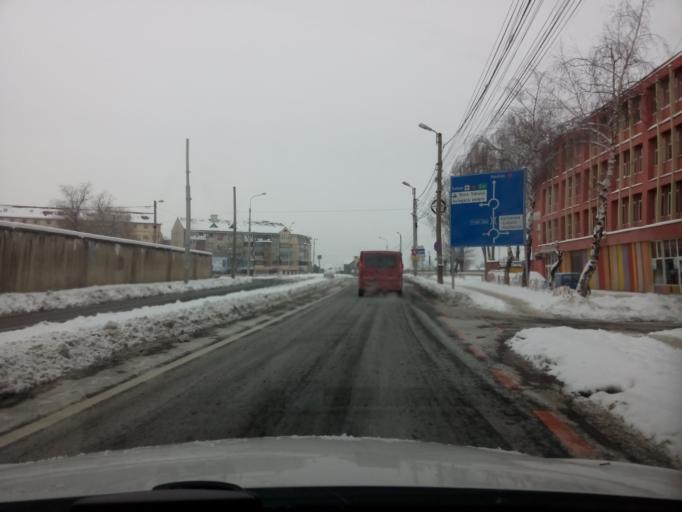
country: RO
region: Sibiu
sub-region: Municipiul Sibiu
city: Sibiu
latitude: 45.8038
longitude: 24.1517
